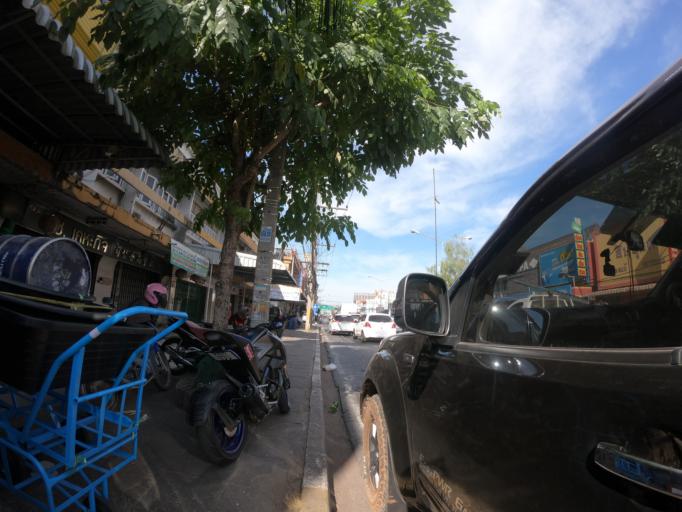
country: TH
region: Khon Kaen
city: Khon Kaen
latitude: 16.4391
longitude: 102.8321
